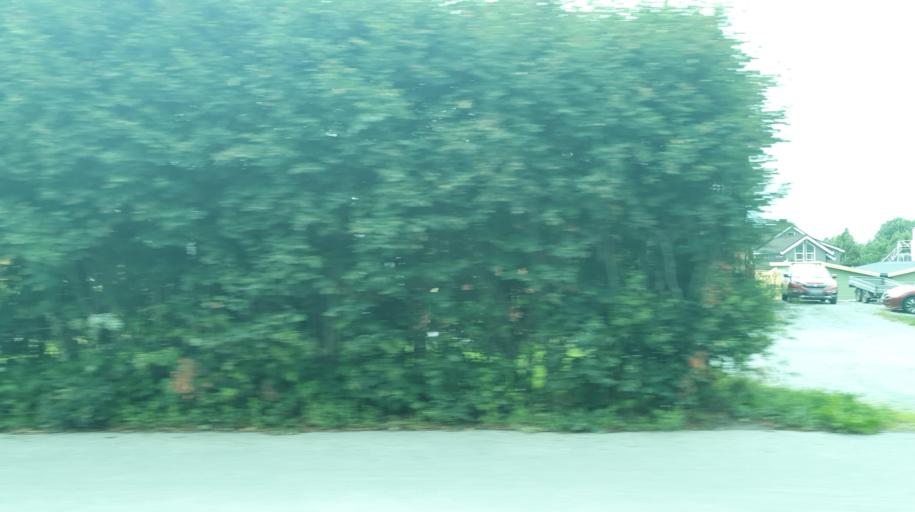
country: NO
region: Sor-Trondelag
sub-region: Trondheim
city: Trondheim
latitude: 63.3577
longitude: 10.3643
